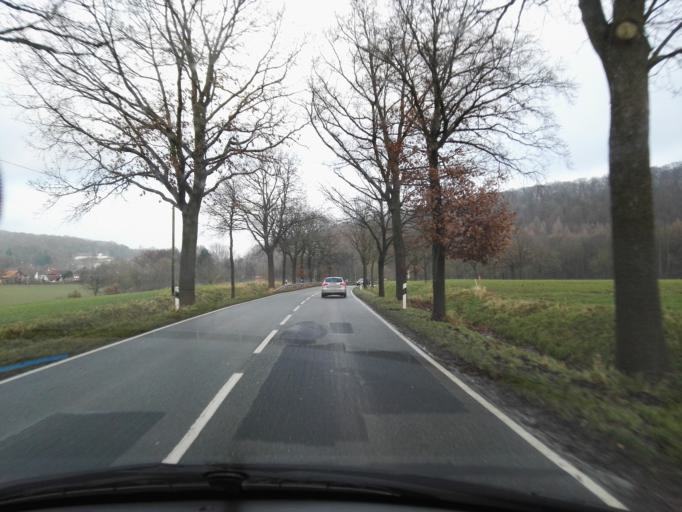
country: DE
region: Lower Saxony
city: Diekholzen
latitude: 52.0868
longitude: 9.9132
